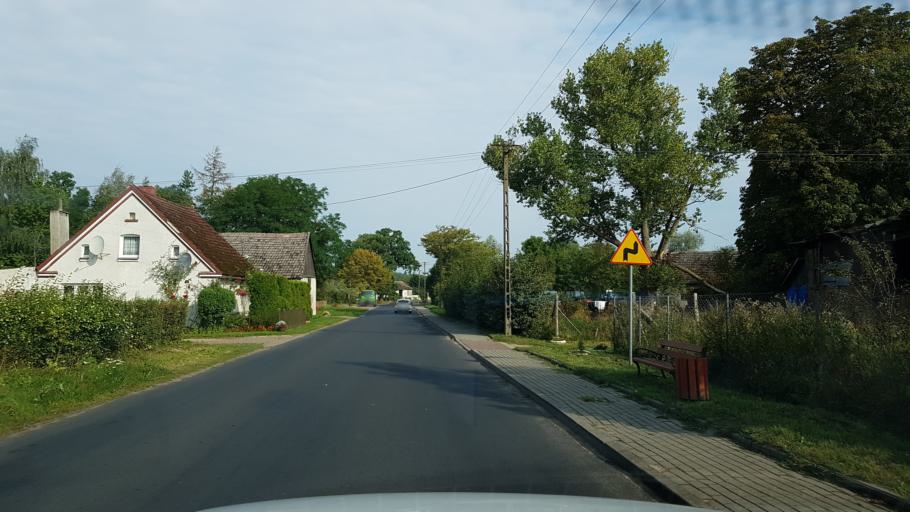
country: PL
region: West Pomeranian Voivodeship
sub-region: Powiat slawienski
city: Slawno
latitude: 54.4629
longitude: 16.5861
